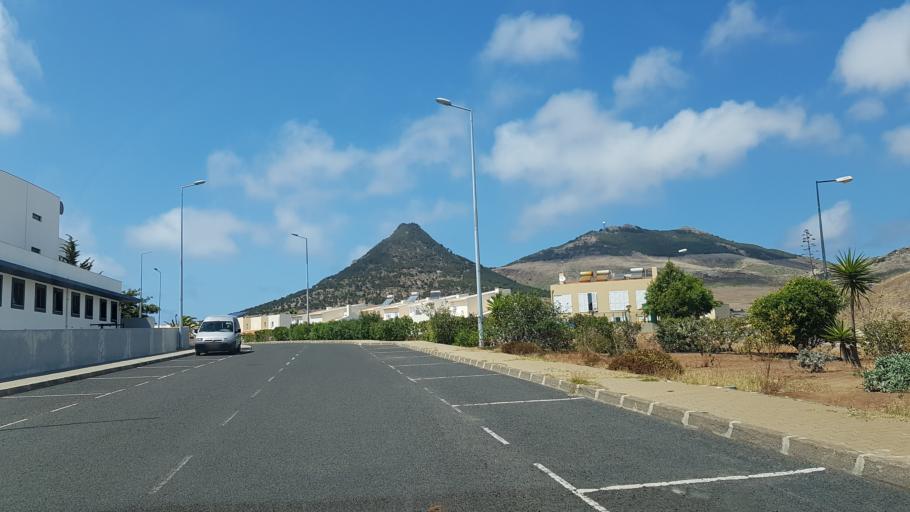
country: PT
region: Madeira
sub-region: Porto Santo
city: Vila de Porto Santo
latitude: 33.0610
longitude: -16.3378
